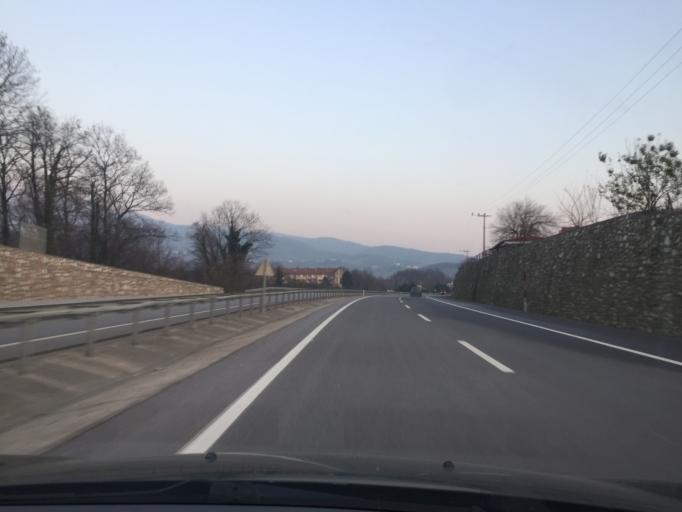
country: TR
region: Sakarya
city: Akyazi
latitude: 40.6262
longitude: 30.6467
